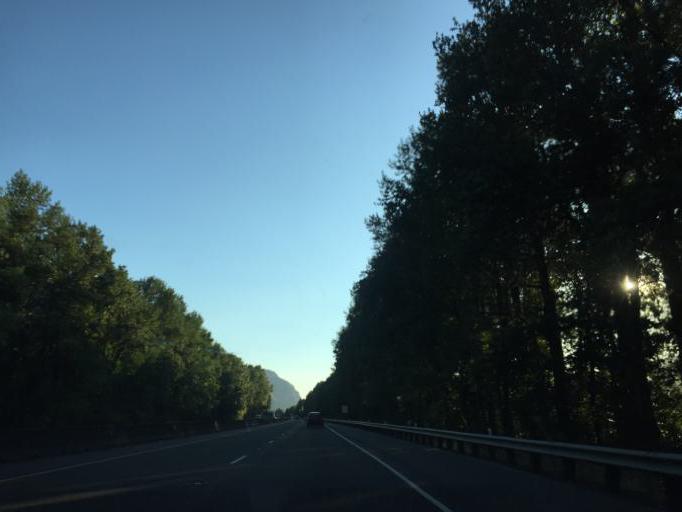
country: US
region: Oregon
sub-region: Hood River County
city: Cascade Locks
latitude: 45.5977
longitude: -122.0596
